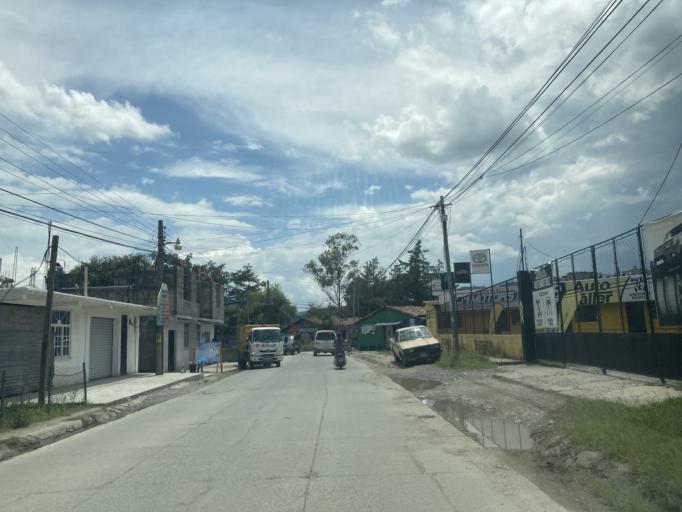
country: GT
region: Huehuetenango
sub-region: Municipio de Huehuetenango
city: Huehuetenango
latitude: 15.3179
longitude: -91.4946
